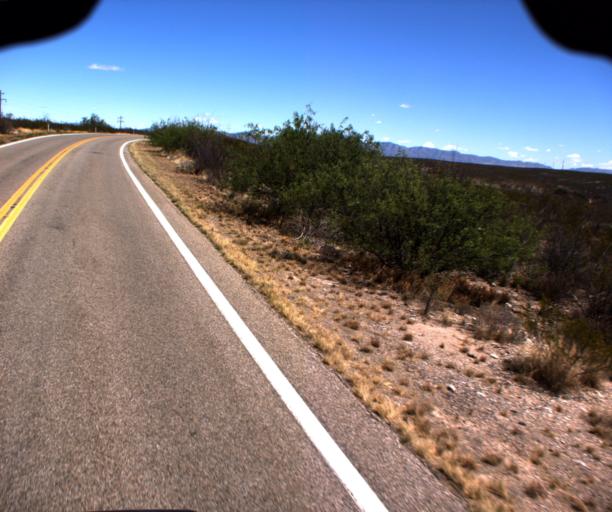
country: US
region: Arizona
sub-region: Cochise County
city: Tombstone
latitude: 31.7345
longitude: -110.1687
